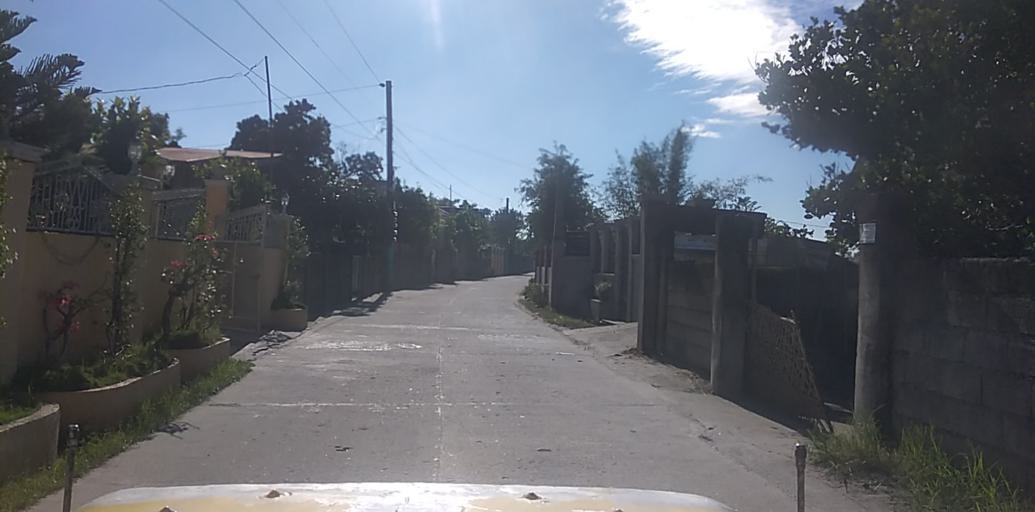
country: PH
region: Central Luzon
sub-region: Province of Pampanga
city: San Patricio
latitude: 15.1152
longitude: 120.7092
